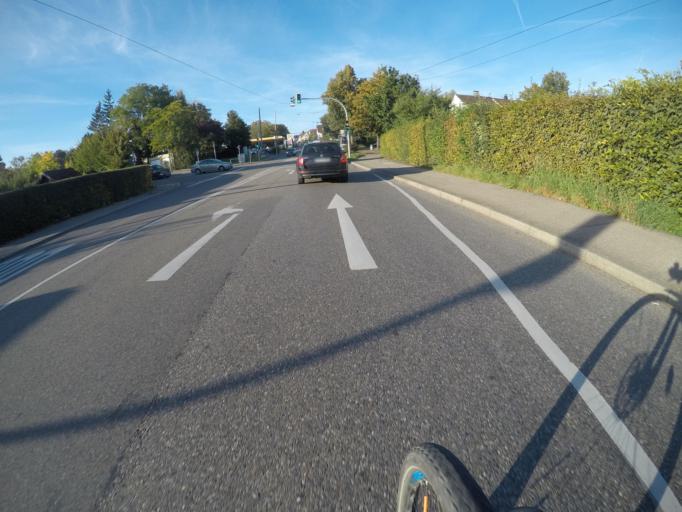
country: DE
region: Baden-Wuerttemberg
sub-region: Regierungsbezirk Stuttgart
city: Stuttgart
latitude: 48.7399
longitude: 9.1693
